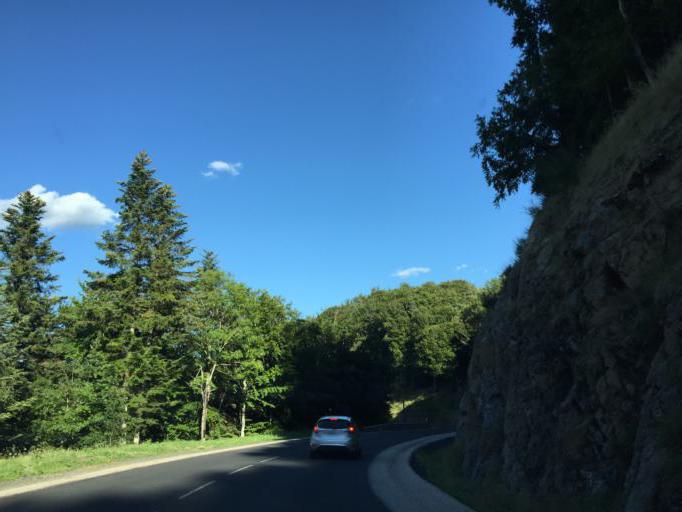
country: FR
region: Auvergne
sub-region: Departement de la Haute-Loire
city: Saugues
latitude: 44.9815
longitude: 3.6209
